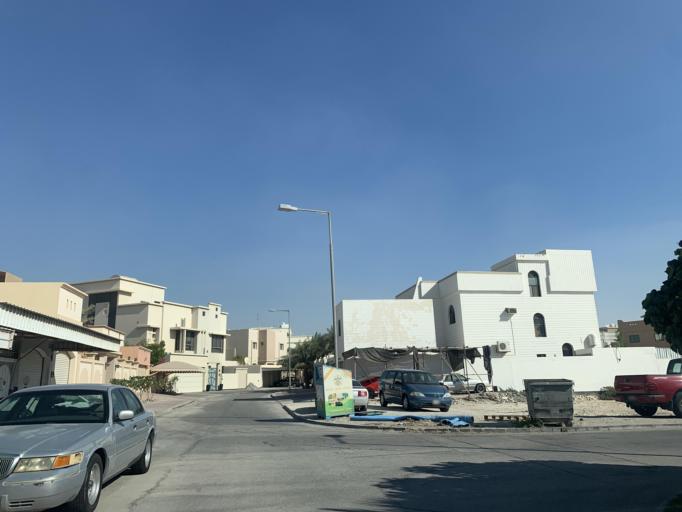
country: BH
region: Central Governorate
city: Madinat Hamad
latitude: 26.1163
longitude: 50.5039
